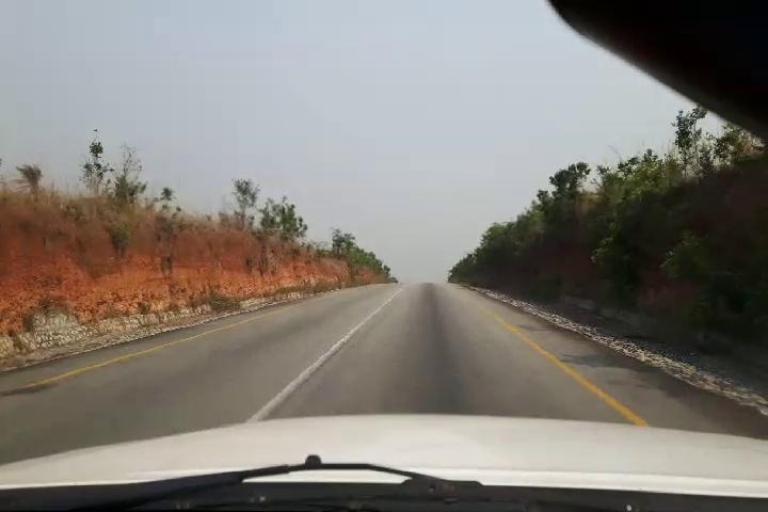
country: SL
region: Southern Province
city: Largo
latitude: 8.2288
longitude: -12.0783
